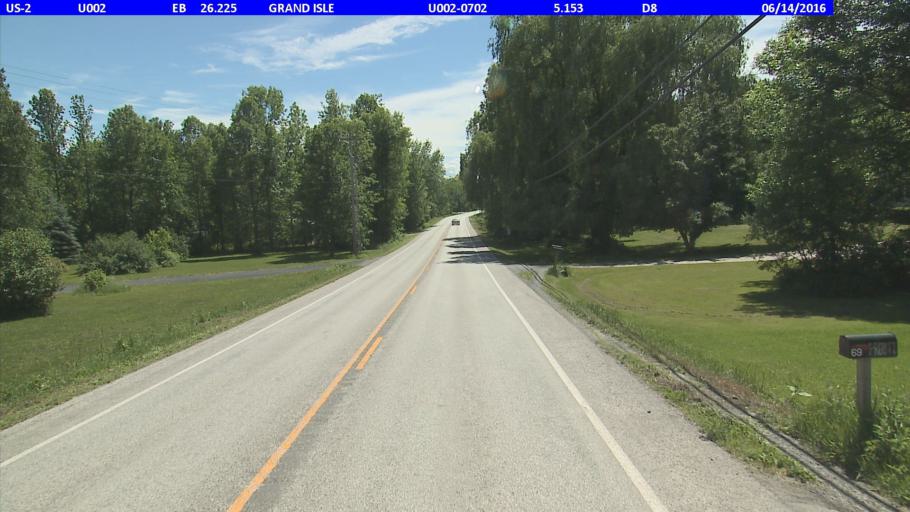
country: US
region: New York
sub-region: Clinton County
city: Cumberland Head
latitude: 44.6948
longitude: -73.3064
